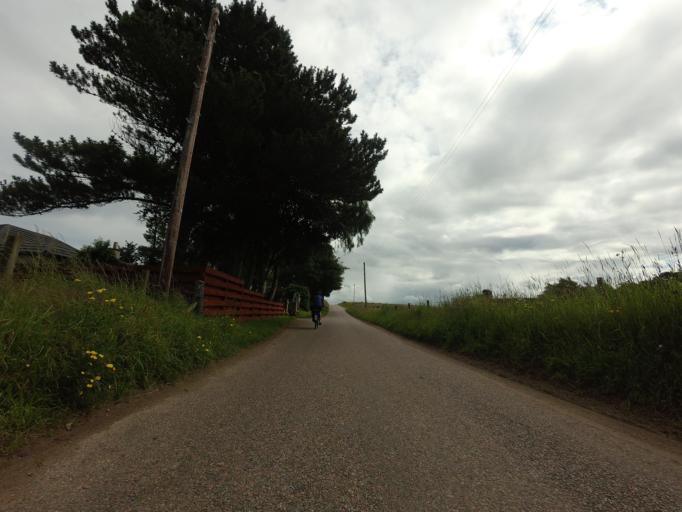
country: GB
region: Scotland
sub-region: Moray
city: Fochabers
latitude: 57.6670
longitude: -3.1492
